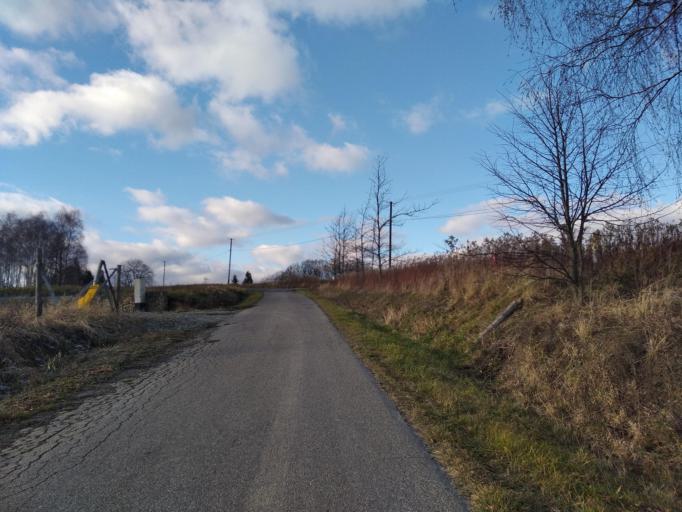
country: PL
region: Subcarpathian Voivodeship
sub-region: Powiat strzyzowski
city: Babica
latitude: 49.9437
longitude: 21.8865
